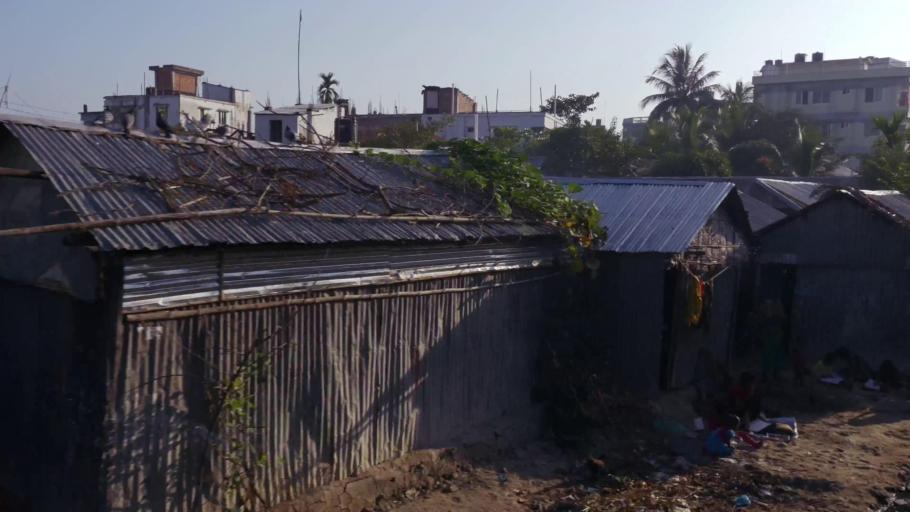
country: BD
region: Dhaka
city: Jamalpur
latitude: 24.8923
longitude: 89.9882
